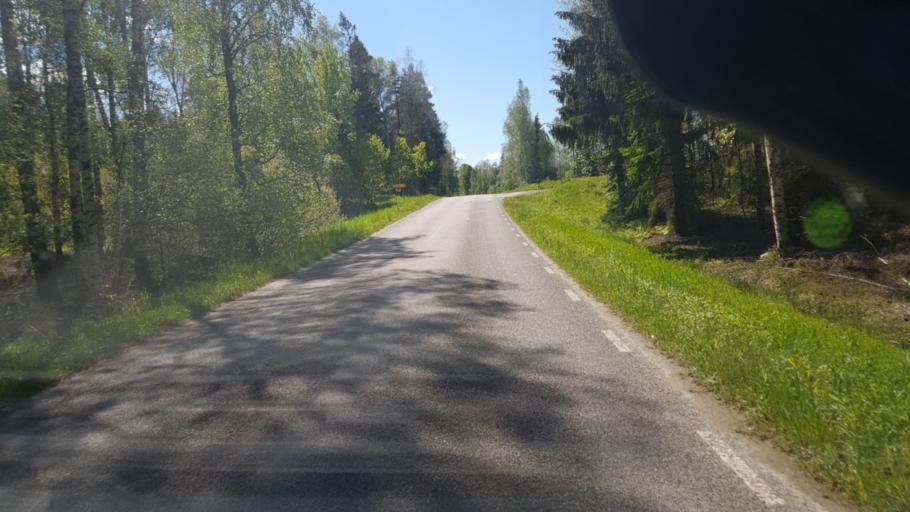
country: SE
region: Vaermland
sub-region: Grums Kommun
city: Slottsbron
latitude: 59.4829
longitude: 12.8831
